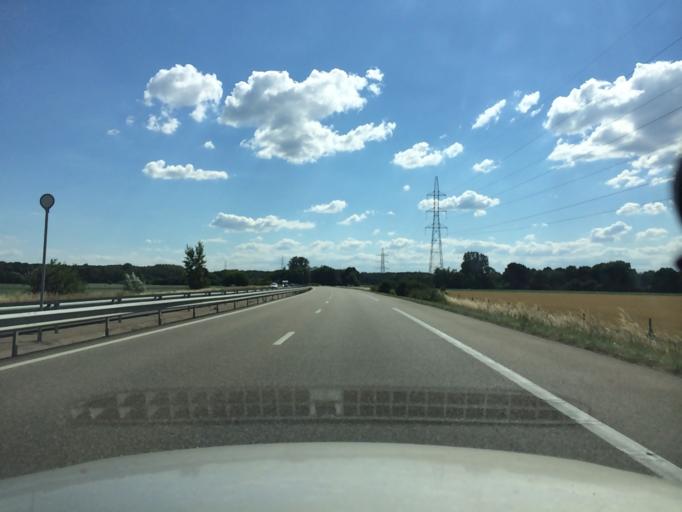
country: FR
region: Alsace
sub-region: Departement du Bas-Rhin
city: Drusenheim
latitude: 48.7709
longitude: 7.9370
